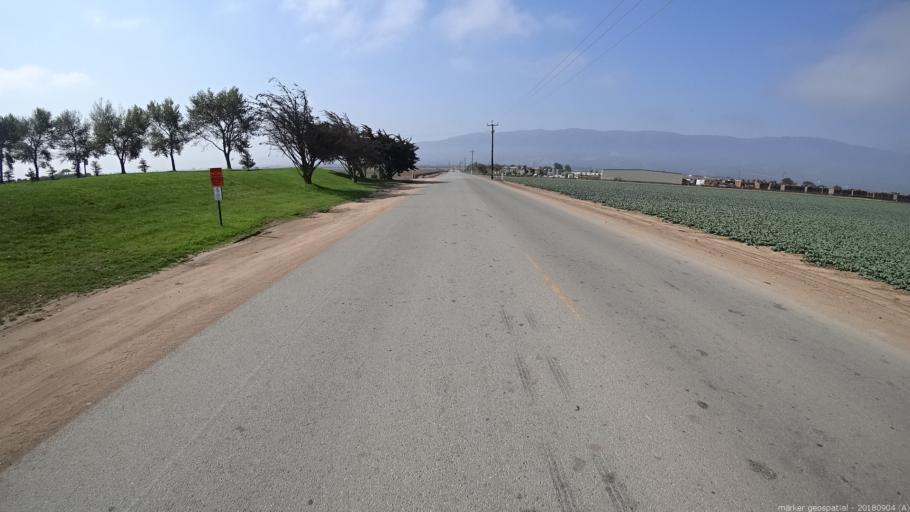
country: US
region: California
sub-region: Monterey County
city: Soledad
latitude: 36.4531
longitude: -121.3573
